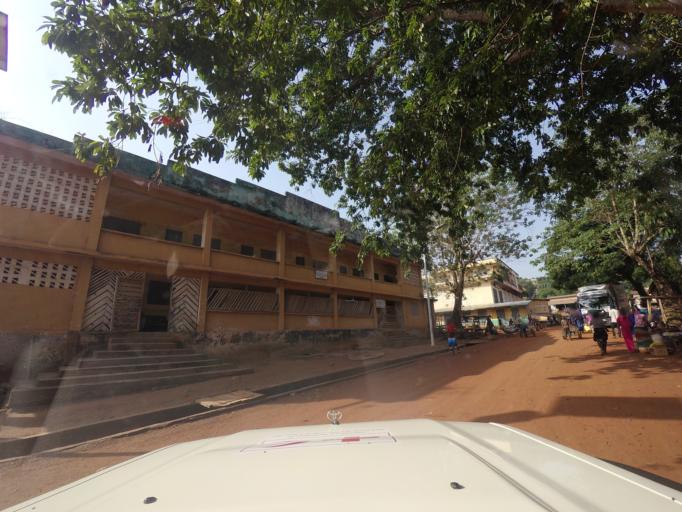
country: GN
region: Nzerekore
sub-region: Prefecture de Guekedou
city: Gueckedou
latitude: 8.5627
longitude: -10.1351
